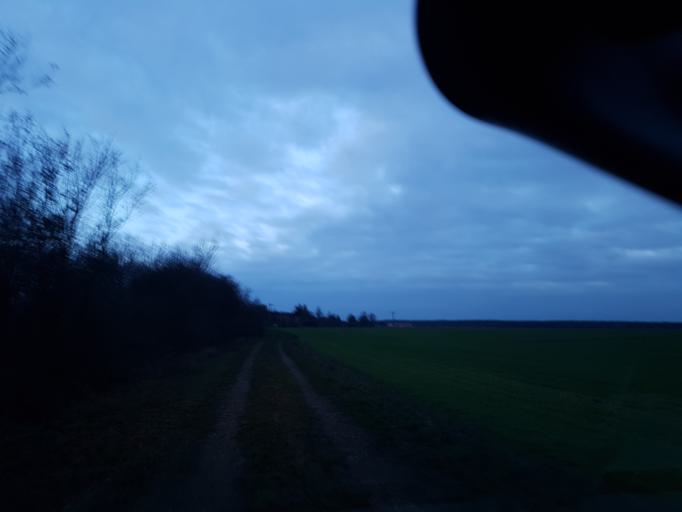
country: DE
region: Brandenburg
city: Muhlberg
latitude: 51.4681
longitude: 13.2685
